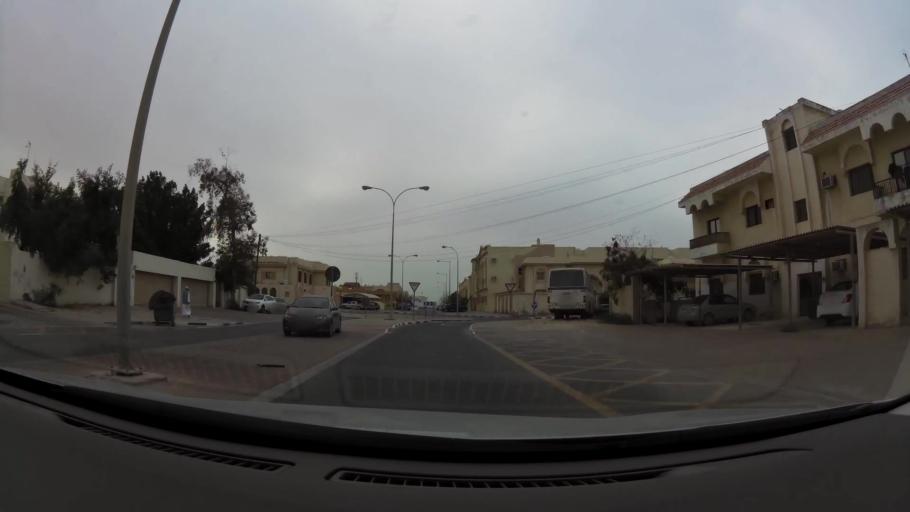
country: QA
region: Baladiyat ad Dawhah
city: Doha
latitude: 25.3106
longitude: 51.4917
